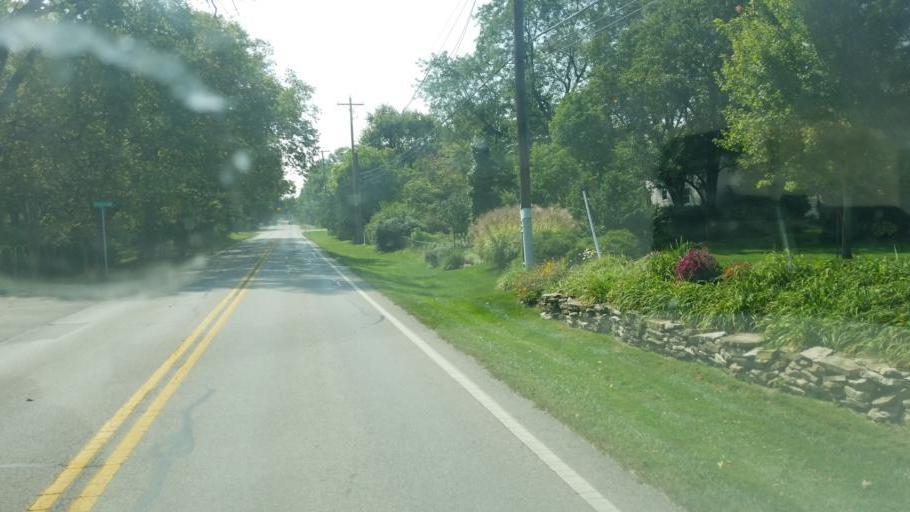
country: US
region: Ohio
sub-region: Franklin County
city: Worthington
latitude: 40.0871
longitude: -83.0388
